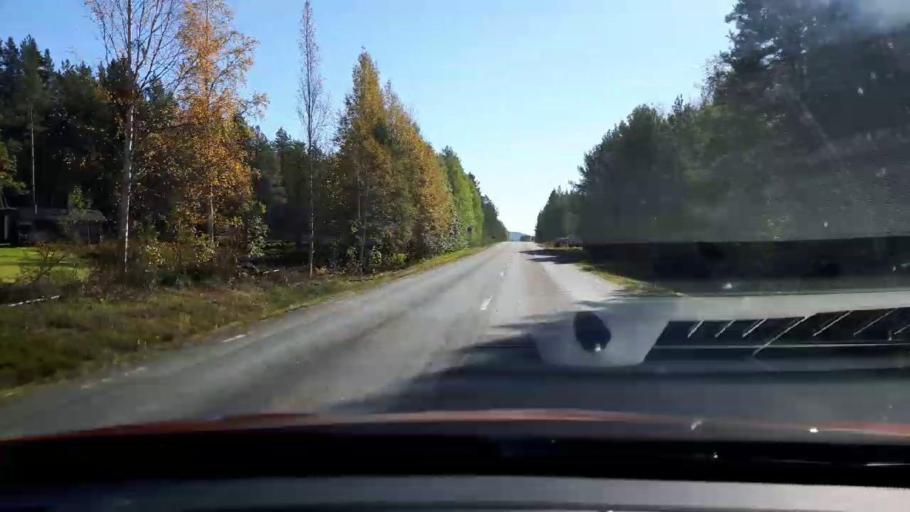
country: SE
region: Jaemtland
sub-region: Harjedalens Kommun
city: Sveg
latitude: 62.3078
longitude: 14.0457
